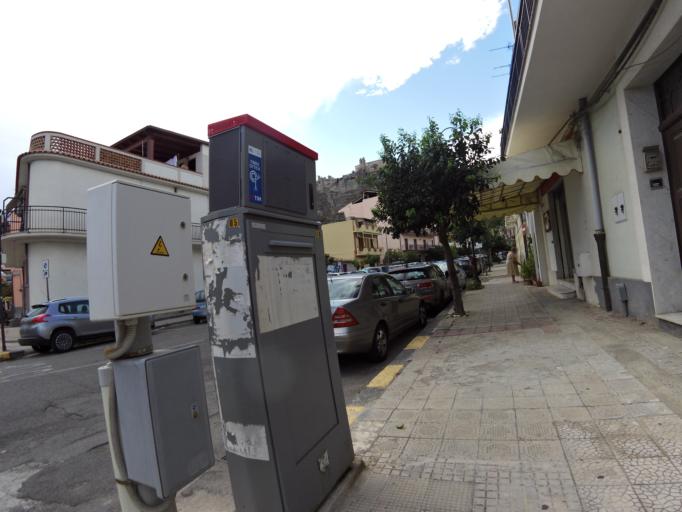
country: IT
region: Calabria
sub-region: Provincia di Reggio Calabria
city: Roccella Ionica
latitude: 38.3239
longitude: 16.4106
